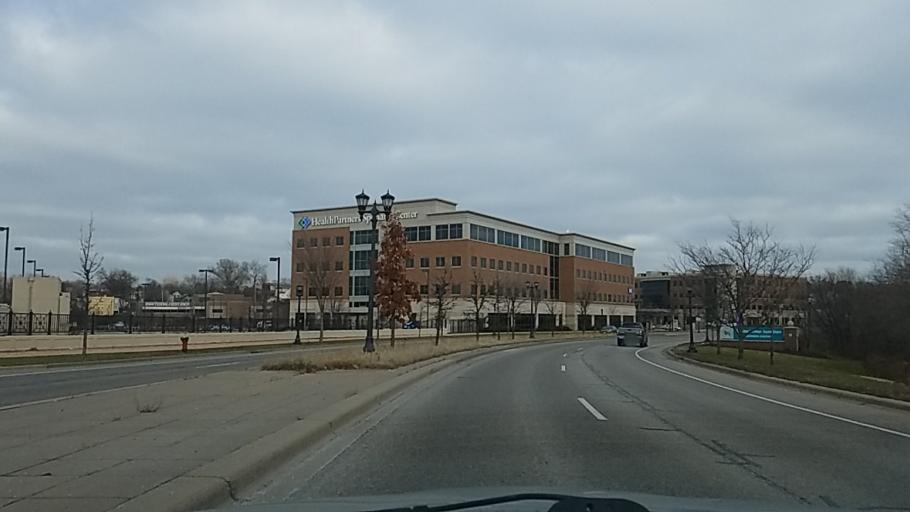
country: US
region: Minnesota
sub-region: Ramsey County
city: Saint Paul
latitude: 44.9636
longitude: -93.0854
